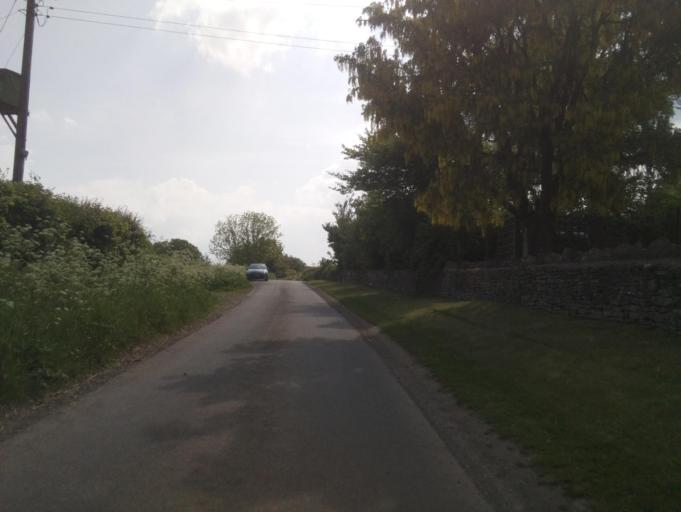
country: GB
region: England
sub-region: South Gloucestershire
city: Horton
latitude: 51.5594
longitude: -2.3365
